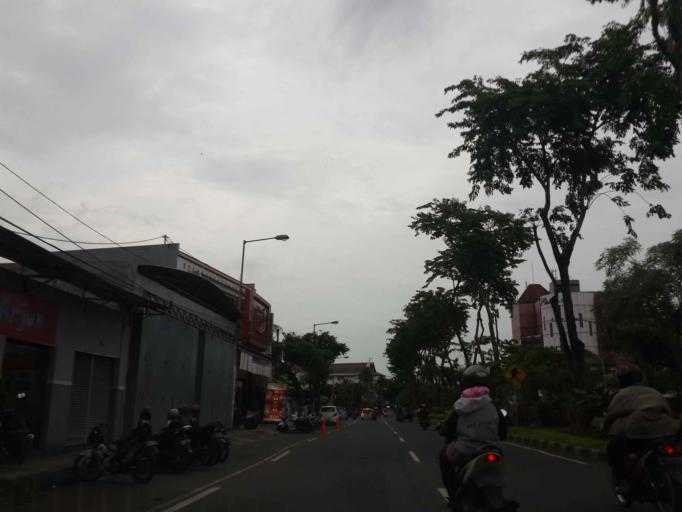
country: ID
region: East Java
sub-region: Kota Surabaya
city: Surabaya
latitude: -7.2659
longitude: 112.7275
